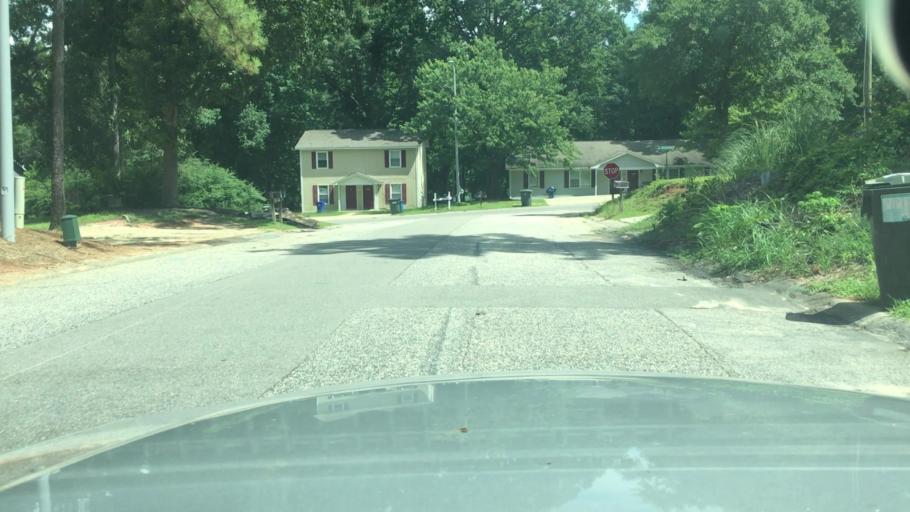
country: US
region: North Carolina
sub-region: Cumberland County
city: Hope Mills
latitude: 35.0339
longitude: -78.9890
